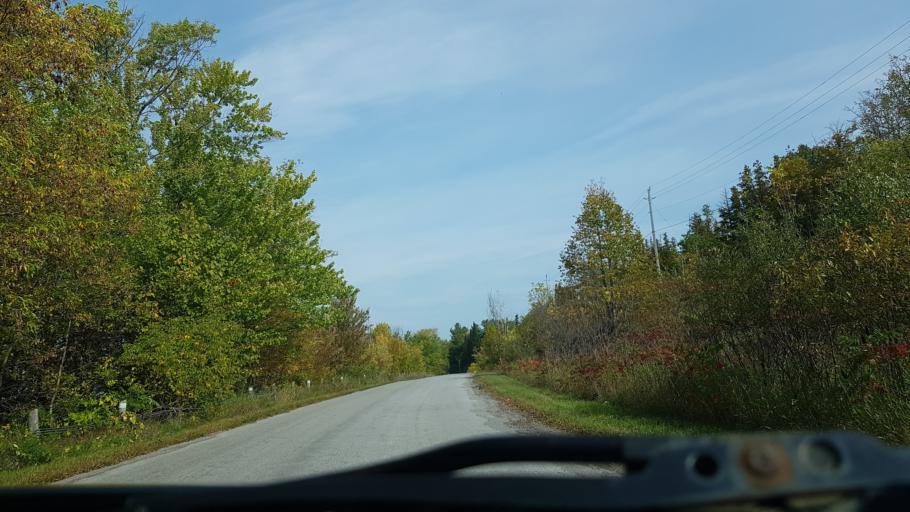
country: CA
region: Ontario
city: Orillia
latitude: 44.6458
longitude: -79.1063
